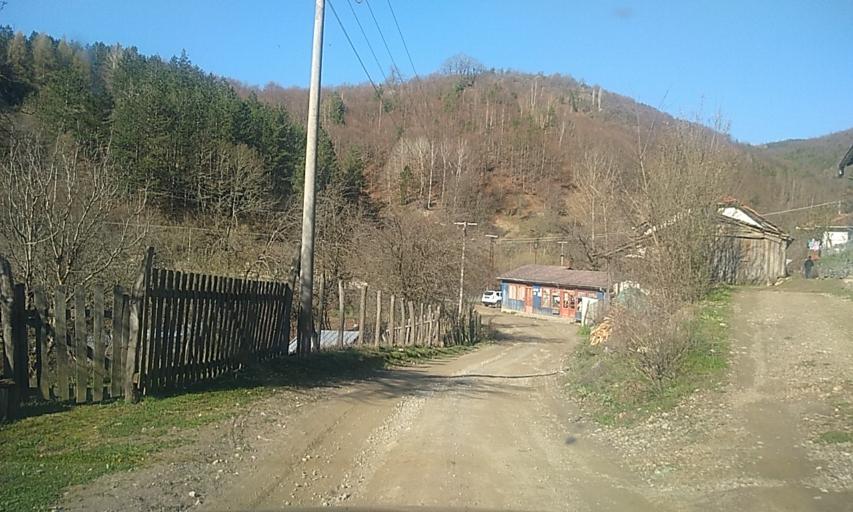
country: RS
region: Central Serbia
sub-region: Pcinjski Okrug
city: Bosilegrad
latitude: 42.3743
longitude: 22.4385
